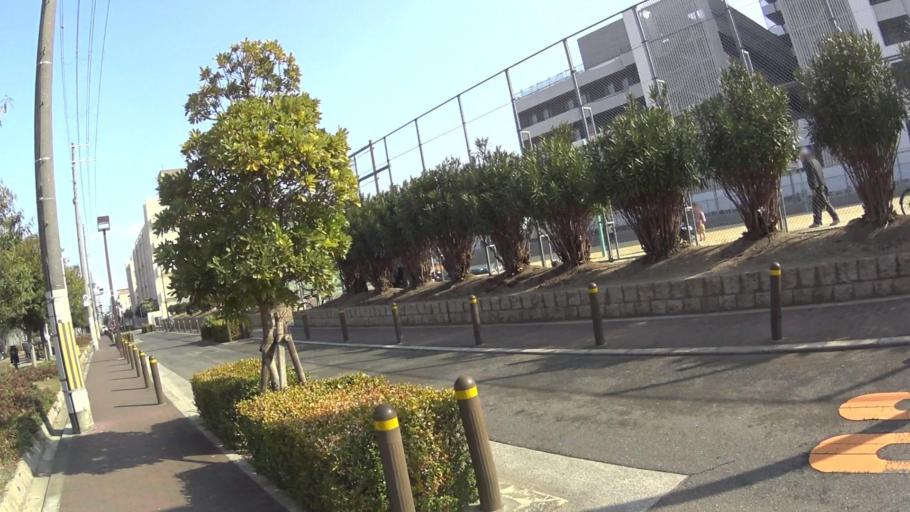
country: JP
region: Osaka
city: Sakai
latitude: 34.6036
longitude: 135.5026
